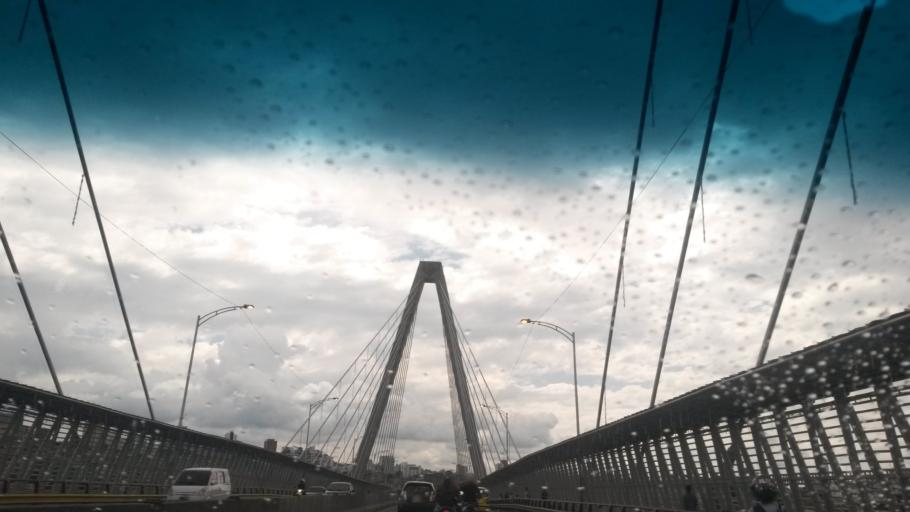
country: CO
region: Risaralda
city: Pereira
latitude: 4.8182
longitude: -75.6861
